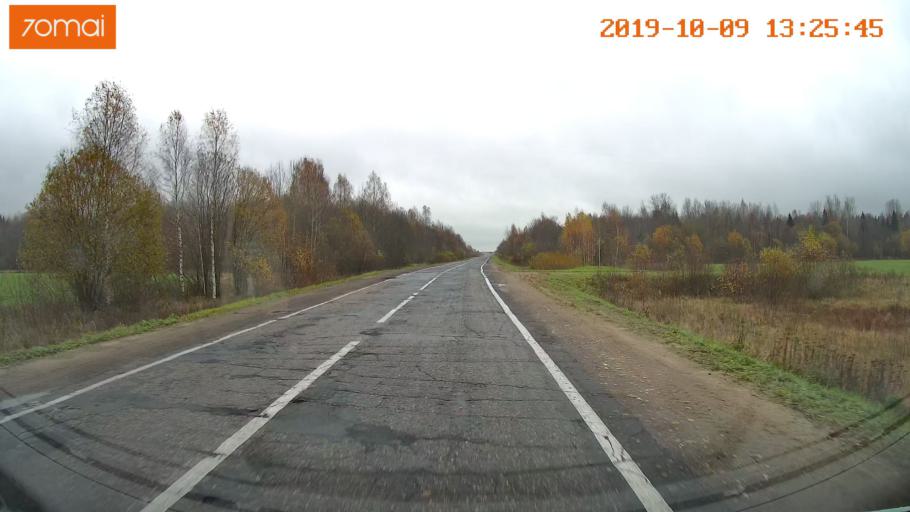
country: RU
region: Jaroslavl
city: Lyubim
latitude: 58.3259
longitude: 40.9157
